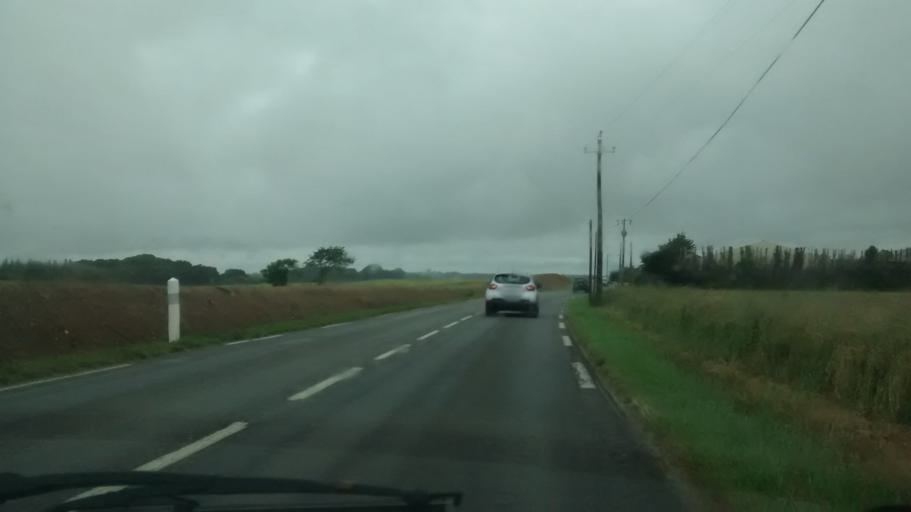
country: FR
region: Brittany
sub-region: Departement du Morbihan
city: Ploemeur
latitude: 47.7534
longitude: -3.4200
